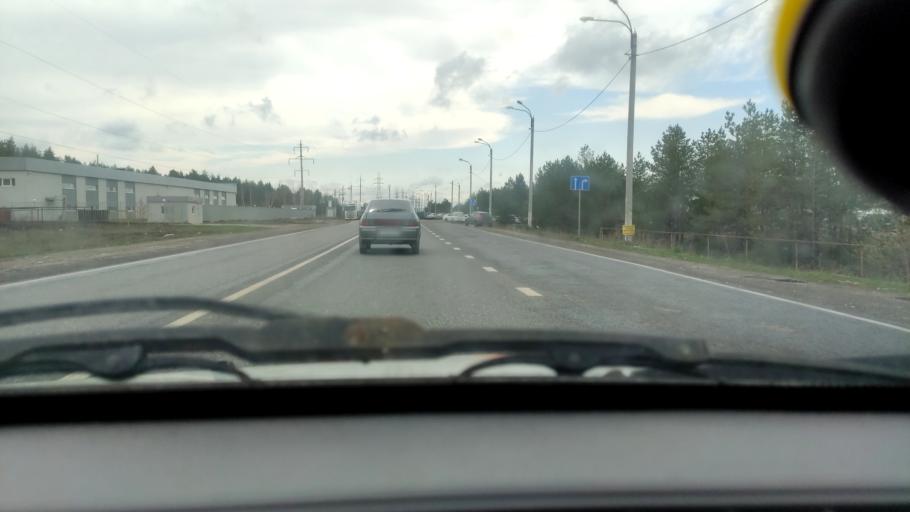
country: RU
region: Samara
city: Zhigulevsk
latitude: 53.5680
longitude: 49.5489
